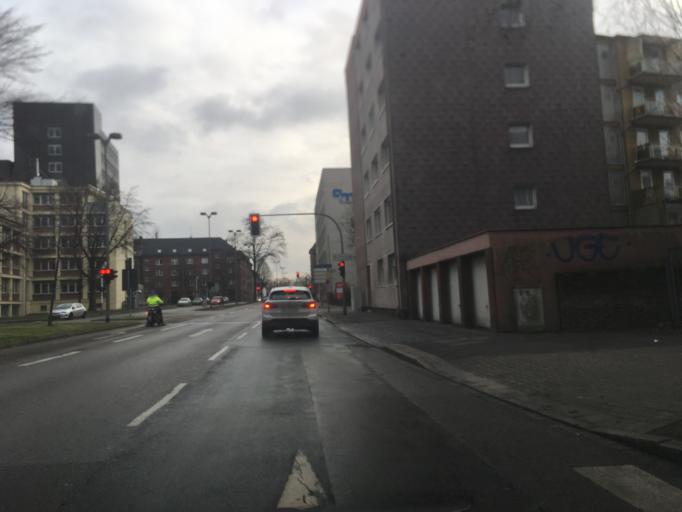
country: DE
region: North Rhine-Westphalia
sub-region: Regierungsbezirk Munster
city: Gelsenkirchen
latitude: 51.5121
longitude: 7.0898
